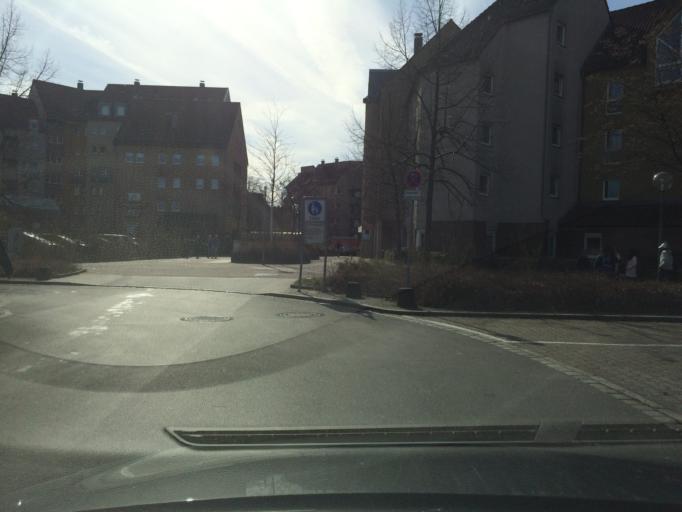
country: DE
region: Bavaria
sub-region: Regierungsbezirk Mittelfranken
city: Nuernberg
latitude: 49.4138
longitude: 11.1239
